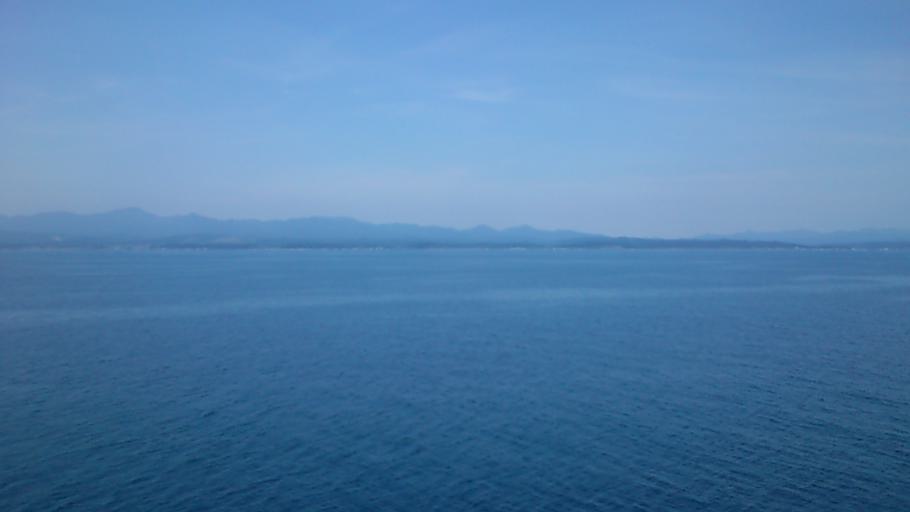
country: JP
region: Aomori
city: Aomori Shi
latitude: 41.0080
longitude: 140.7245
